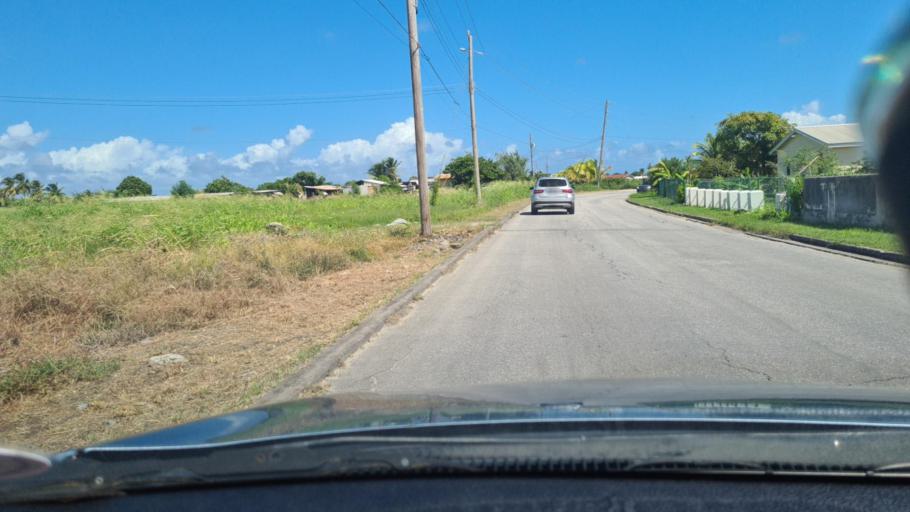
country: BB
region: Saint Philip
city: Crane
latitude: 13.1300
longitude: -59.4467
